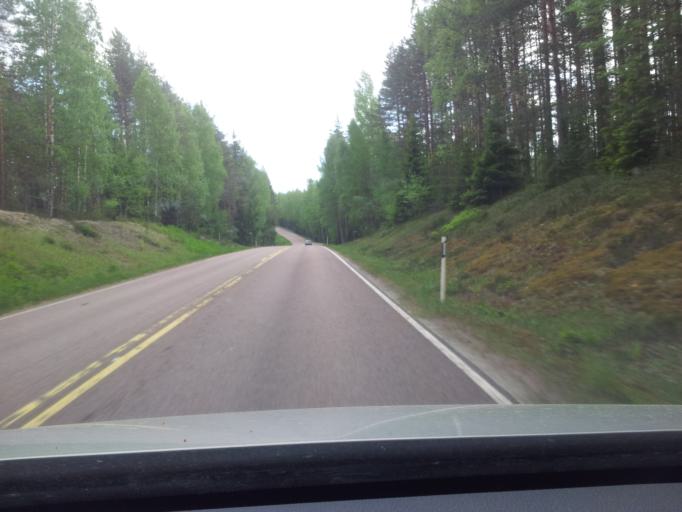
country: FI
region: South Karelia
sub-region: Lappeenranta
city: Luumaeki
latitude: 60.9701
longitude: 27.5597
